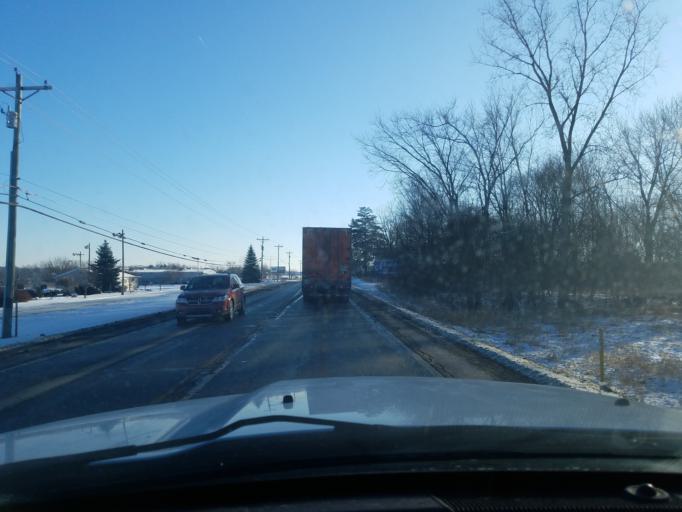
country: US
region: Indiana
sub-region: Noble County
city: Kendallville
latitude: 41.4524
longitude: -85.3026
